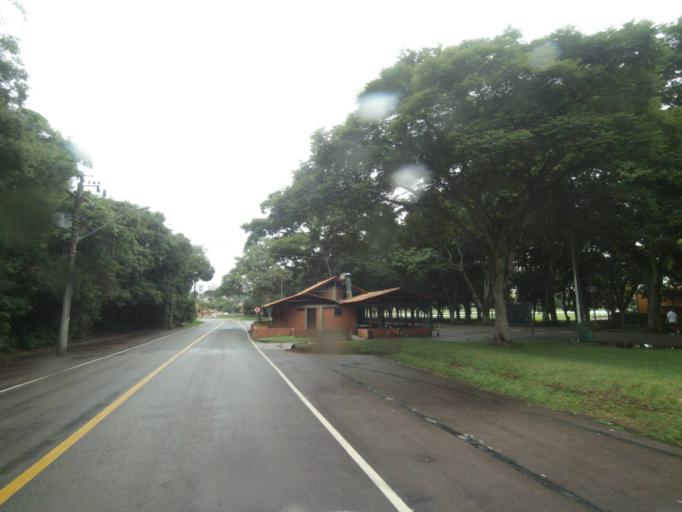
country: BR
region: Parana
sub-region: Curitiba
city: Curitiba
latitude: -25.4269
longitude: -49.3103
